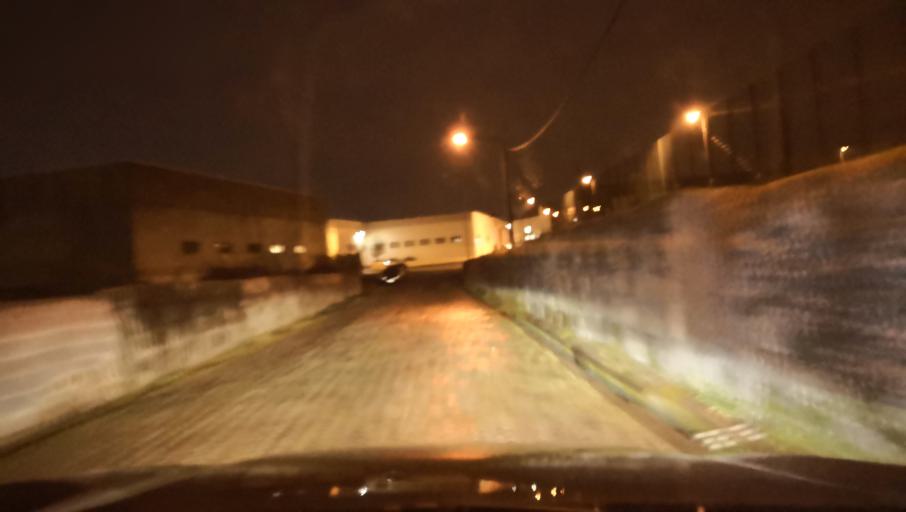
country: PT
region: Porto
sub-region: Matosinhos
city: Guifoes
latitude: 41.2025
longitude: -8.6856
